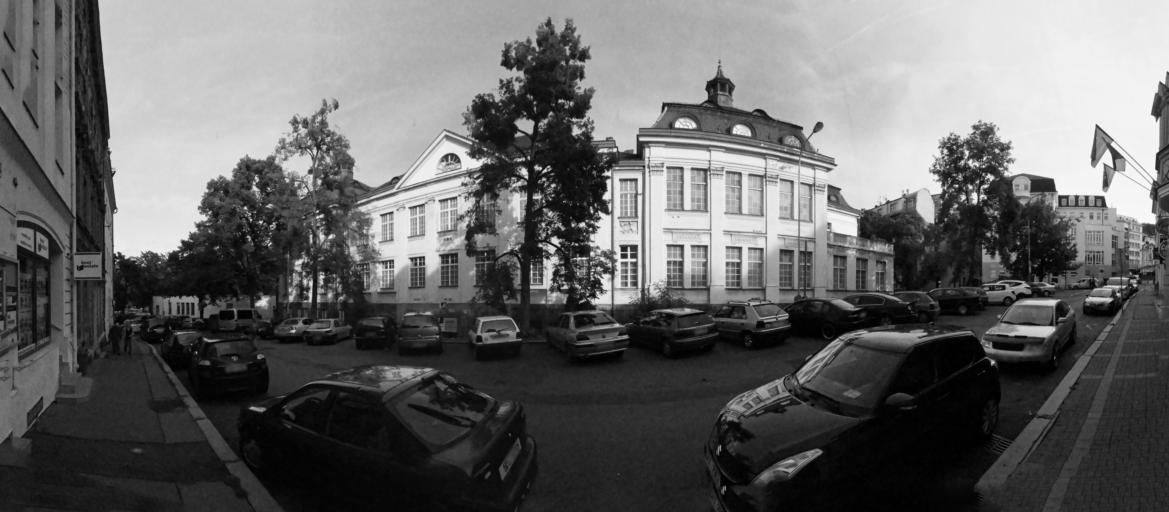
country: CZ
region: Karlovarsky
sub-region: Okres Karlovy Vary
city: Karlovy Vary
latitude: 50.2303
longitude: 12.8714
